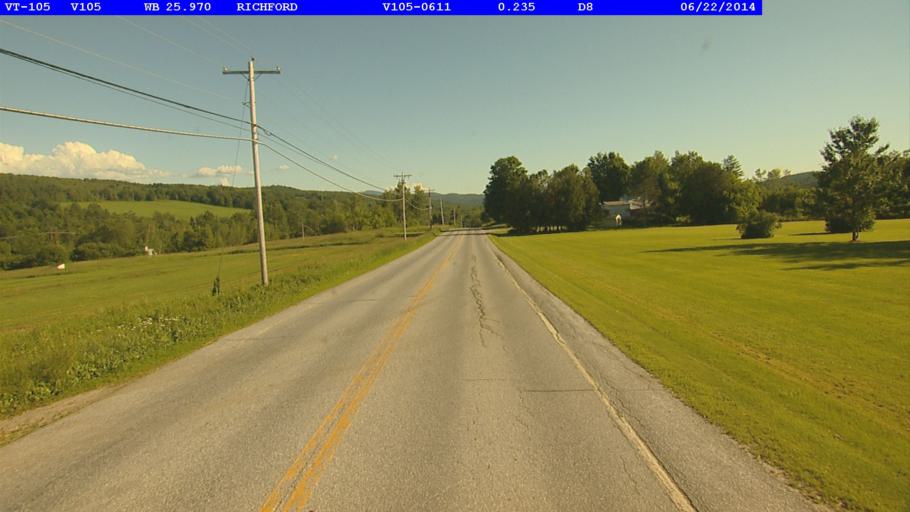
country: US
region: Vermont
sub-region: Franklin County
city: Richford
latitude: 44.9746
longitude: -72.6882
